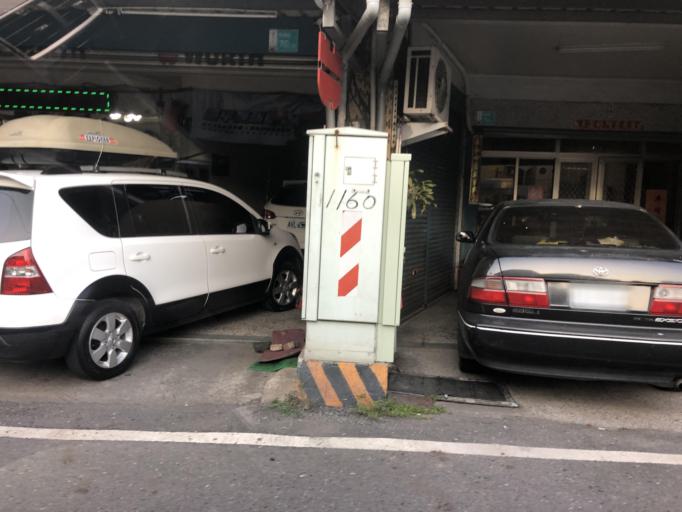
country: TW
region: Taiwan
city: Xinying
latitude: 23.1786
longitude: 120.2525
